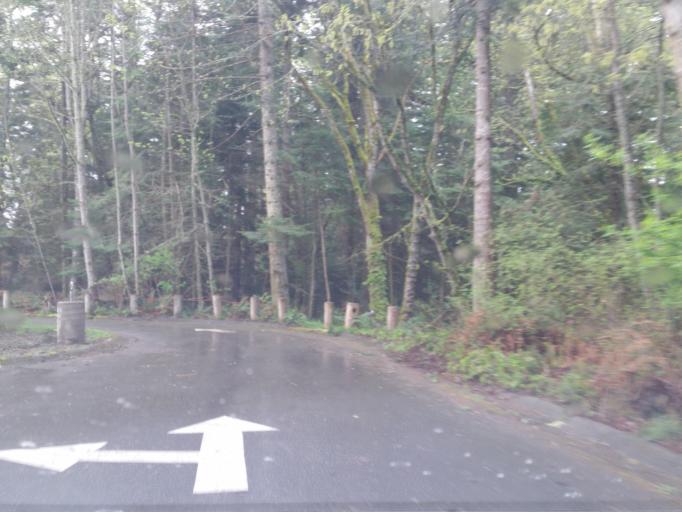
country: CA
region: British Columbia
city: Colwood
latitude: 48.4341
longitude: -123.4548
